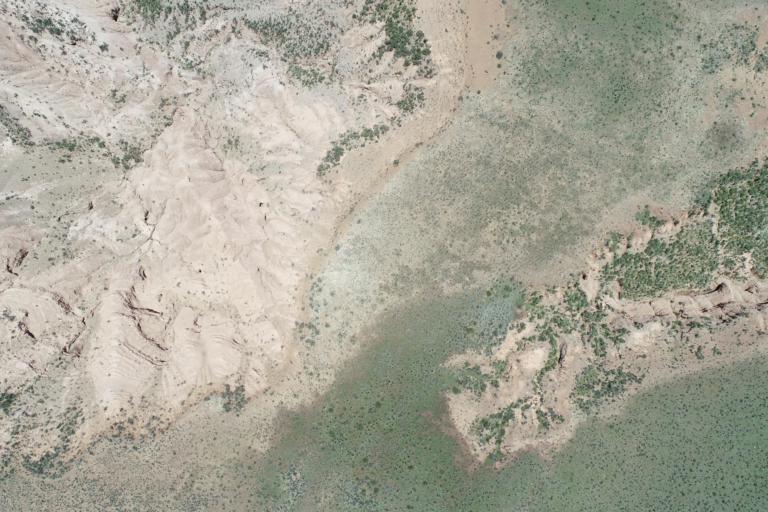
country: BO
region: La Paz
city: Curahuara de Carangas
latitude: -17.3063
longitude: -68.5002
